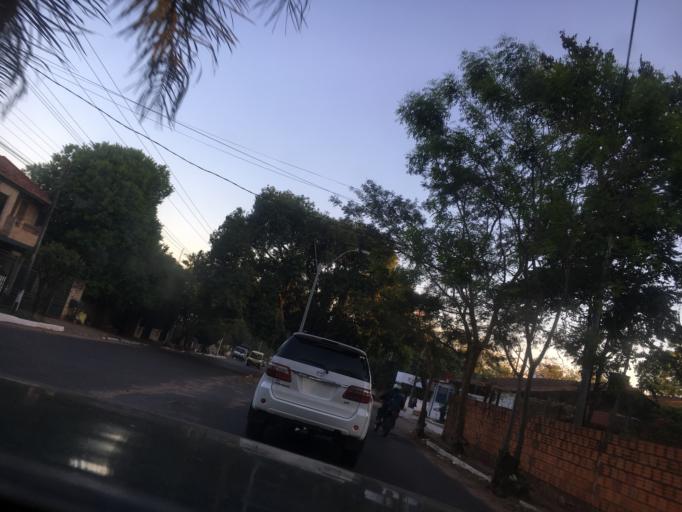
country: PY
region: Central
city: Lambare
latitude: -25.3291
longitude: -57.6097
